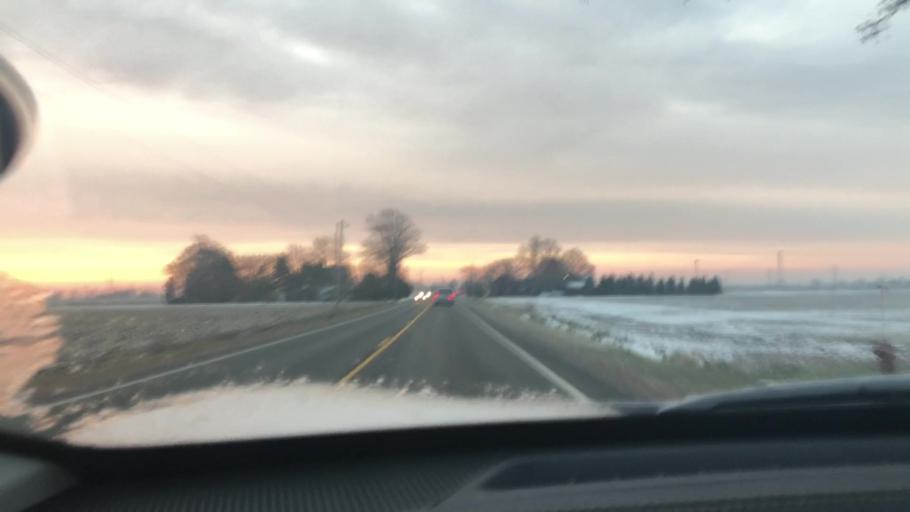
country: US
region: Michigan
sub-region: Saginaw County
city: Zilwaukee
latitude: 43.5102
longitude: -83.8362
